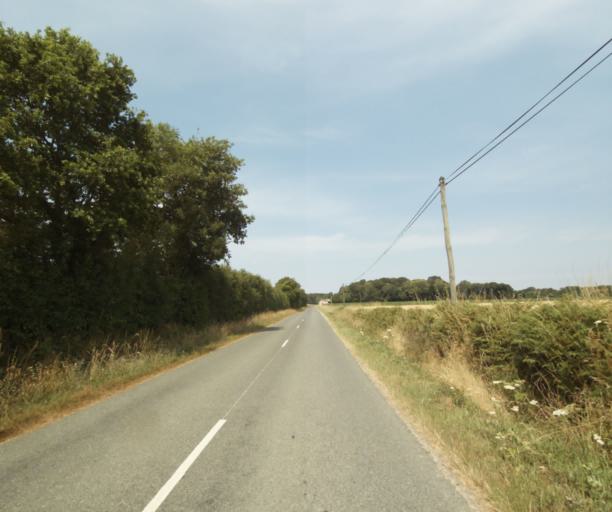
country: FR
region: Centre
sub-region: Departement d'Eure-et-Loir
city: Authon-du-Perche
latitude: 48.1838
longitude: 0.9371
